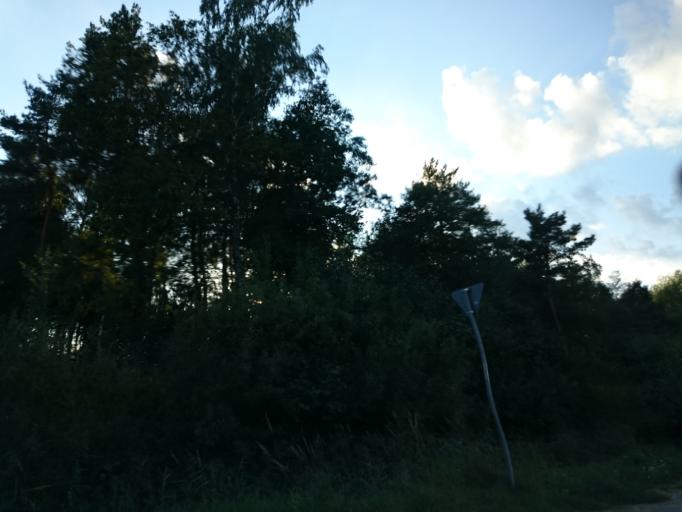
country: LV
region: Adazi
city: Adazi
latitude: 57.0744
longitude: 24.2788
